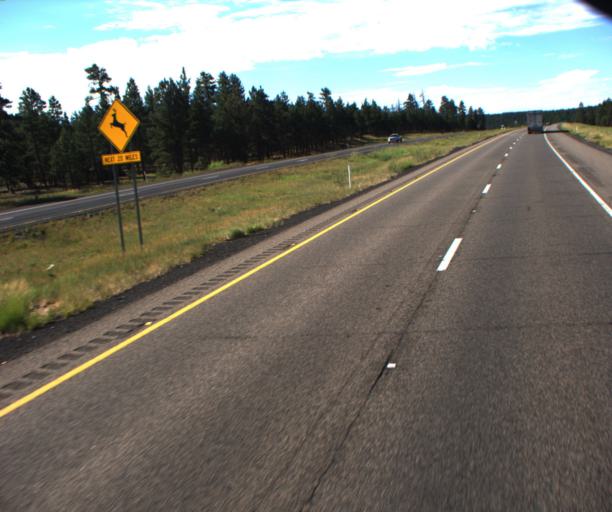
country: US
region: Arizona
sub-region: Coconino County
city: Sedona
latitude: 34.8944
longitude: -111.6415
